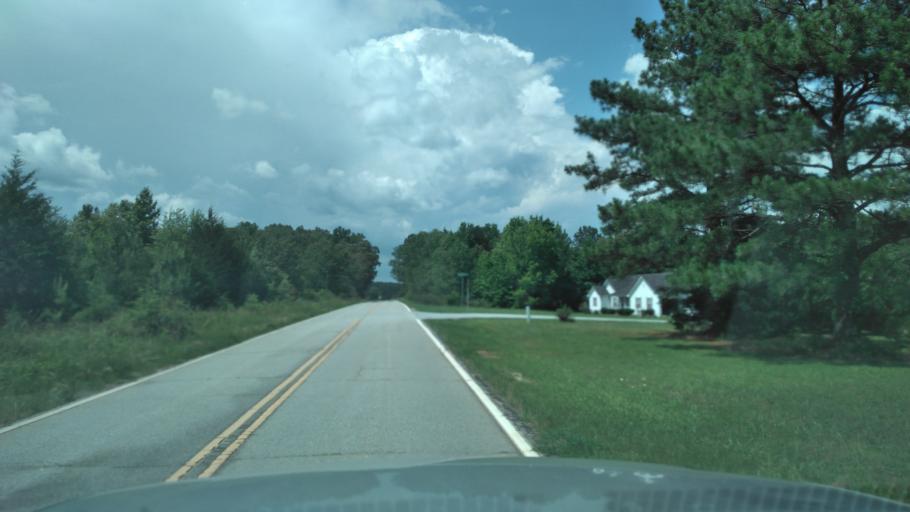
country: US
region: South Carolina
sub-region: Laurens County
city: Laurens
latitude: 34.4977
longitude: -82.0940
